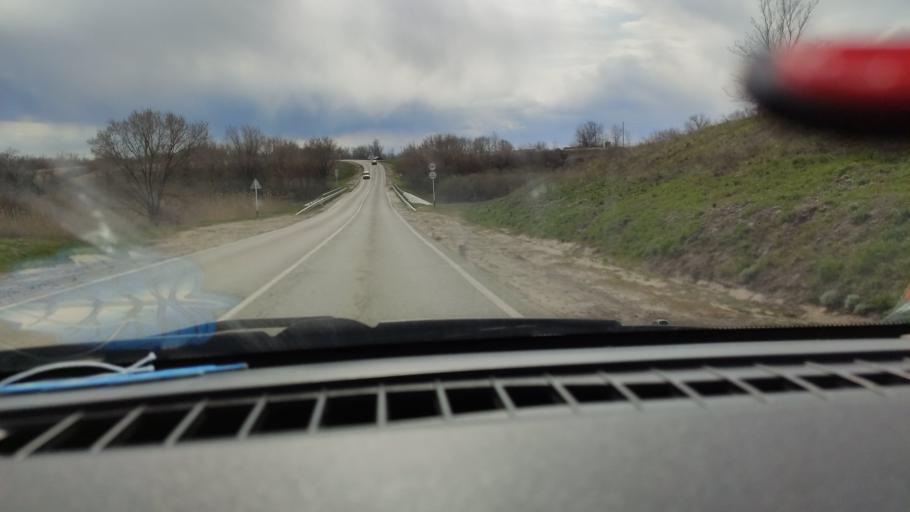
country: RU
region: Saratov
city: Privolzhskiy
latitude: 51.3302
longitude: 46.0345
